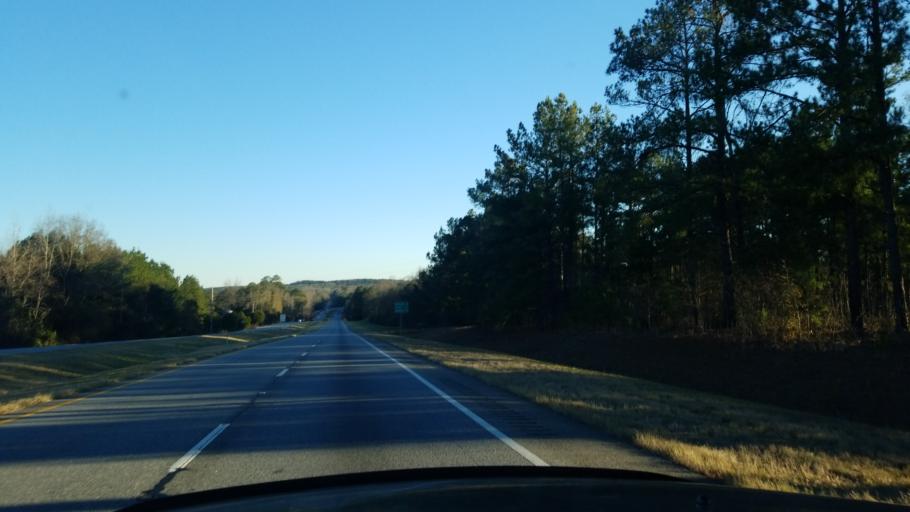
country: US
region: Georgia
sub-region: Chattahoochee County
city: Cusseta
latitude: 32.2895
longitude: -84.7666
